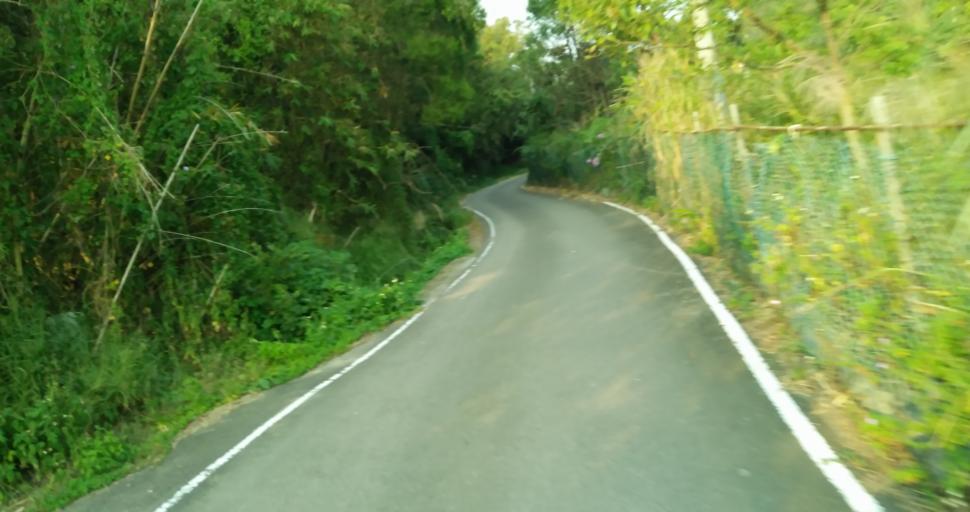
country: TW
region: Taiwan
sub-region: Hsinchu
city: Hsinchu
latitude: 24.7615
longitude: 120.9635
